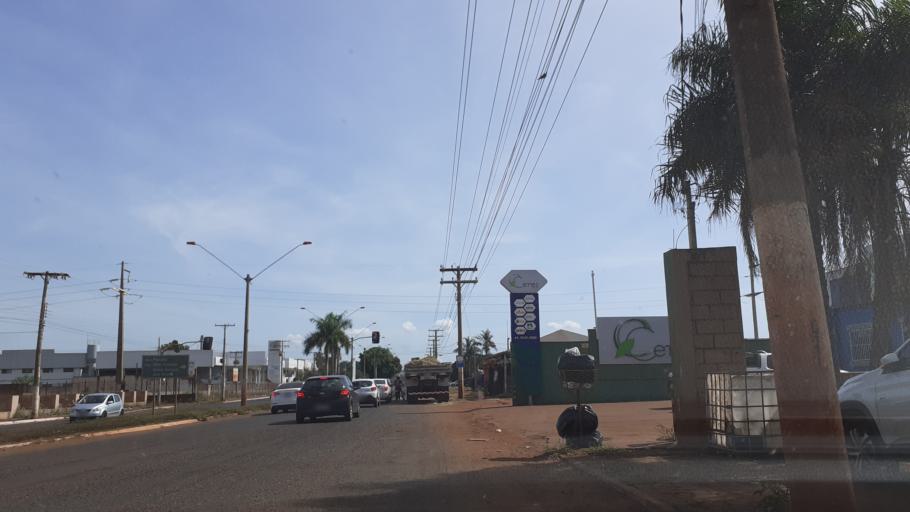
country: BR
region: Goias
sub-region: Itumbiara
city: Itumbiara
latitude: -18.4130
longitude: -49.2423
